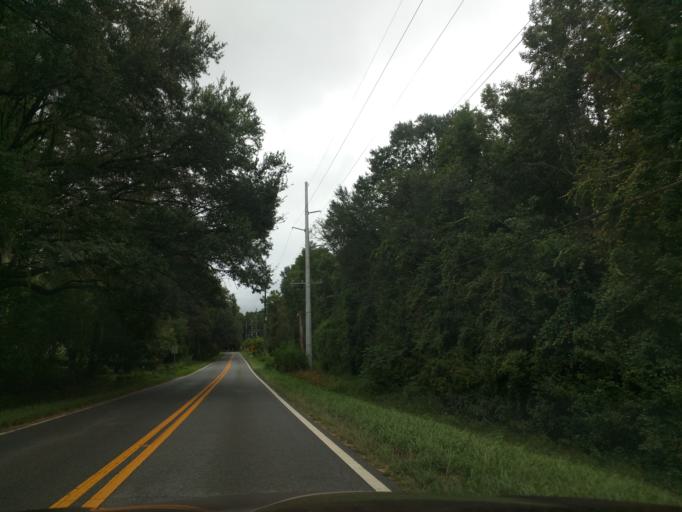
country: US
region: Florida
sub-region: Leon County
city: Tallahassee
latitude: 30.5103
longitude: -84.1256
